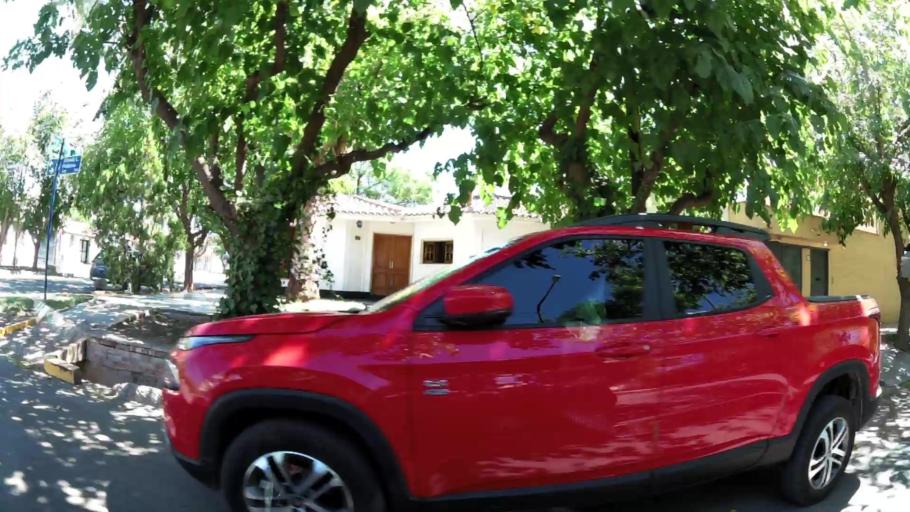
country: AR
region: Mendoza
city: Las Heras
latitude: -32.8504
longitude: -68.8506
